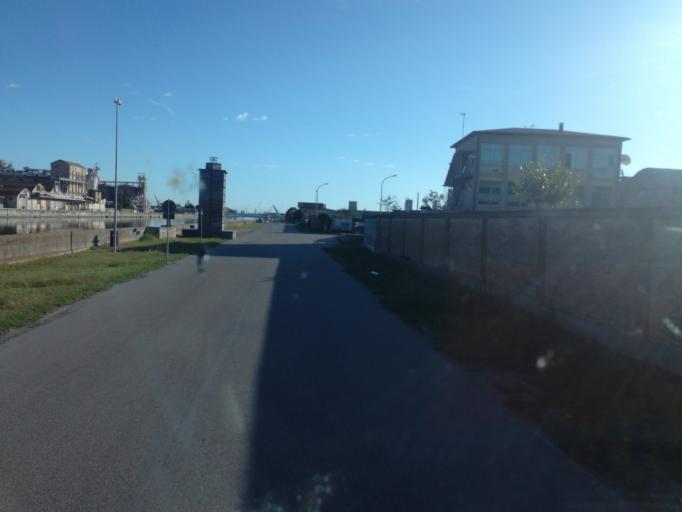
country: IT
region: Emilia-Romagna
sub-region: Provincia di Ravenna
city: Ravenna
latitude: 44.4249
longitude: 12.2190
